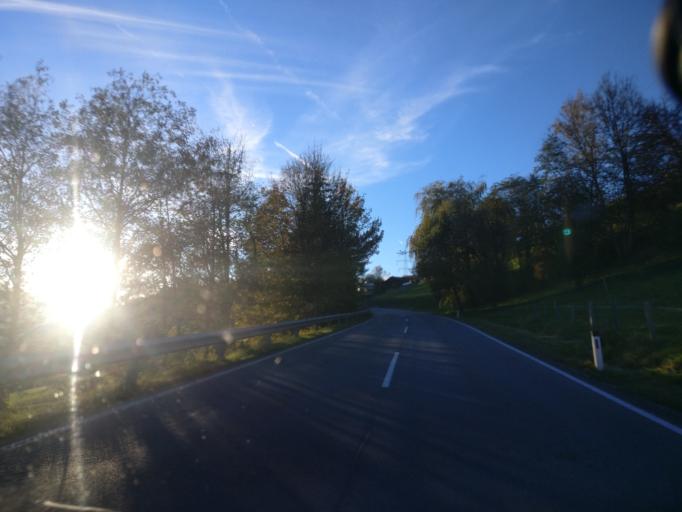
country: AT
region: Salzburg
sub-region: Politischer Bezirk Sankt Johann im Pongau
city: Schwarzach im Pongau
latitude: 47.3250
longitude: 13.1541
